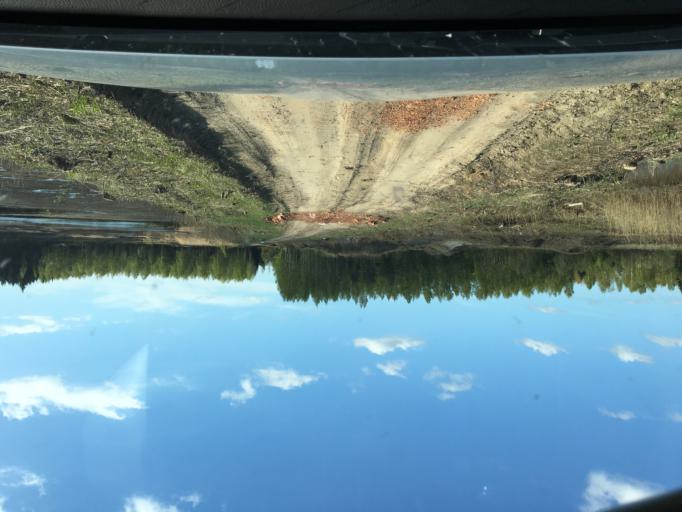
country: LV
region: Ozolnieku
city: Ozolnieki
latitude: 56.6648
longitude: 23.8657
